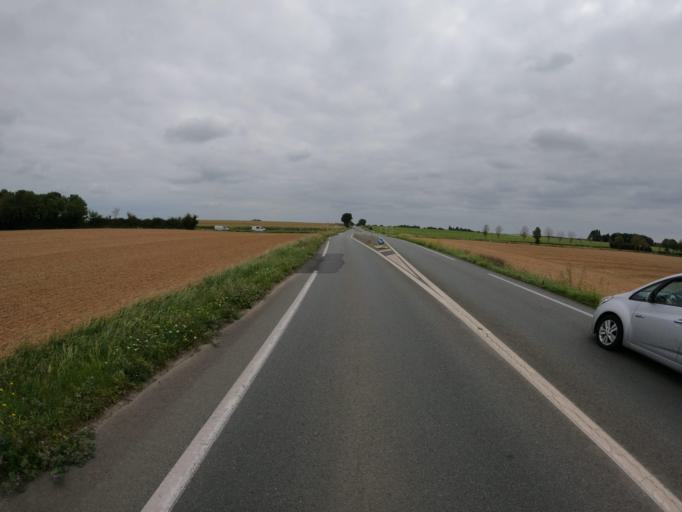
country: FR
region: Pays de la Loire
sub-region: Departement de la Vendee
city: Sainte-Hermine
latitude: 46.5337
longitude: -1.0119
